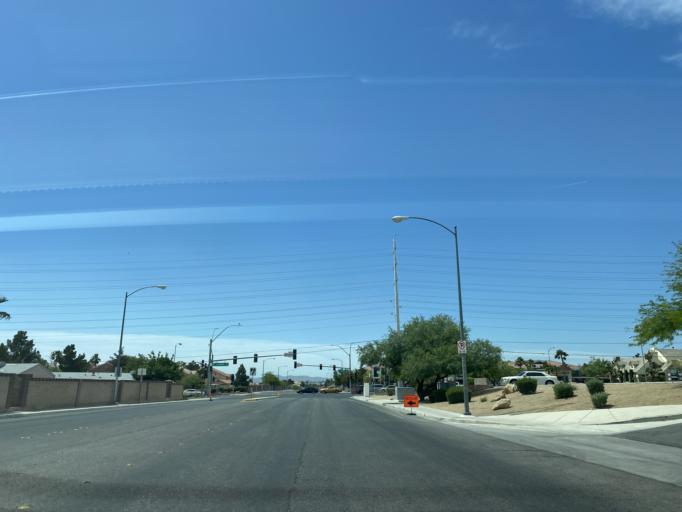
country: US
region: Nevada
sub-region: Clark County
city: Spring Valley
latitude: 36.1158
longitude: -115.2700
